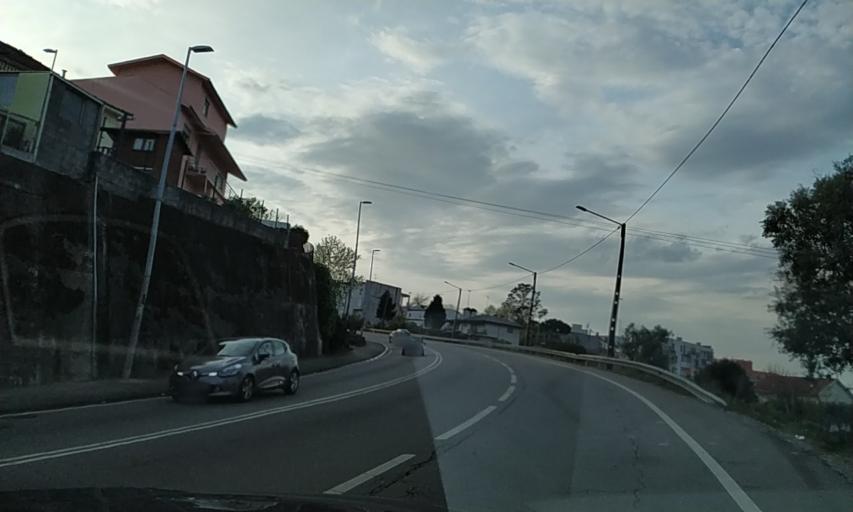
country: PT
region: Porto
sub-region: Valongo
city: Valongo
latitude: 41.1910
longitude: -8.5068
